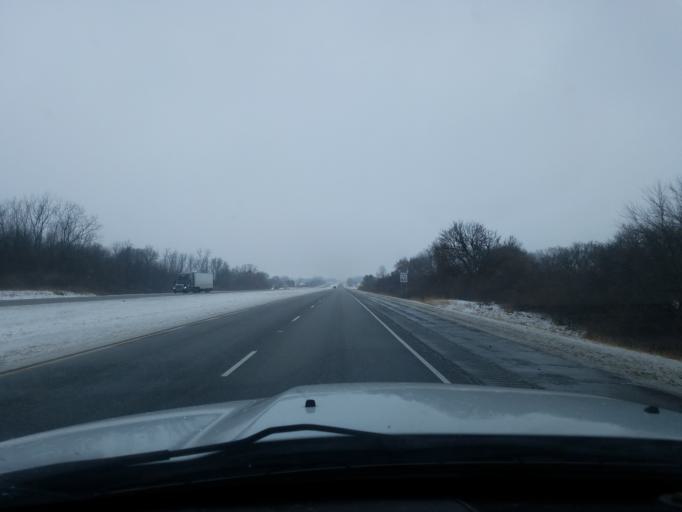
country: US
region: Indiana
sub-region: Fulton County
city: Rochester
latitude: 40.9400
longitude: -86.1683
